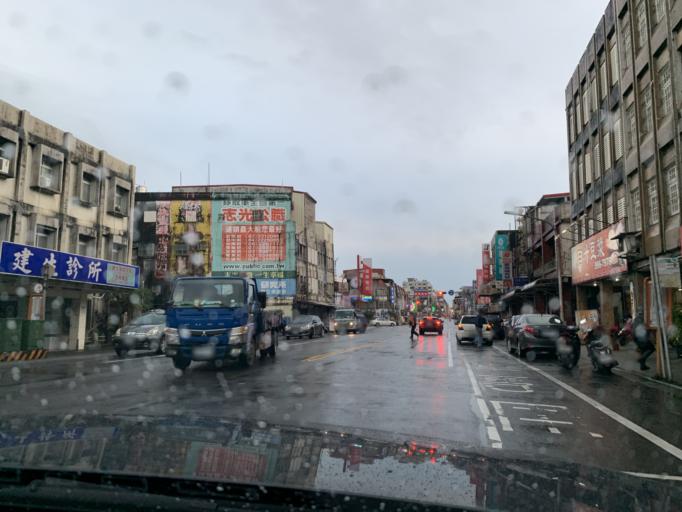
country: TW
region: Taiwan
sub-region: Yilan
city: Yilan
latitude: 24.5958
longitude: 121.8460
